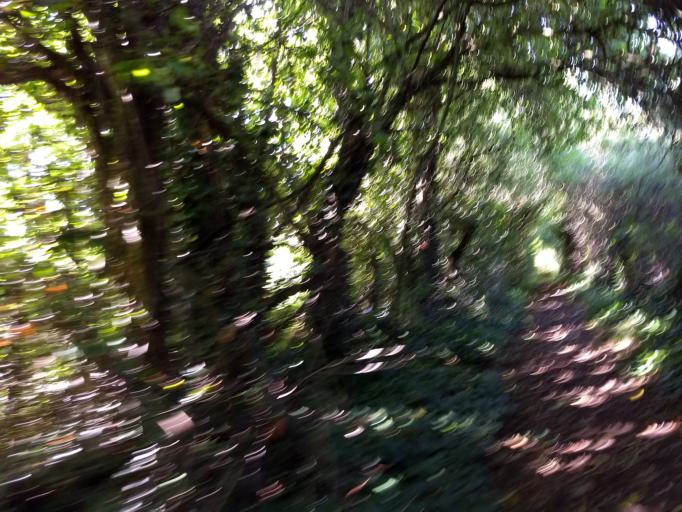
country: GB
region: England
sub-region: Isle of Wight
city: Ryde
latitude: 50.7148
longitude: -1.1605
